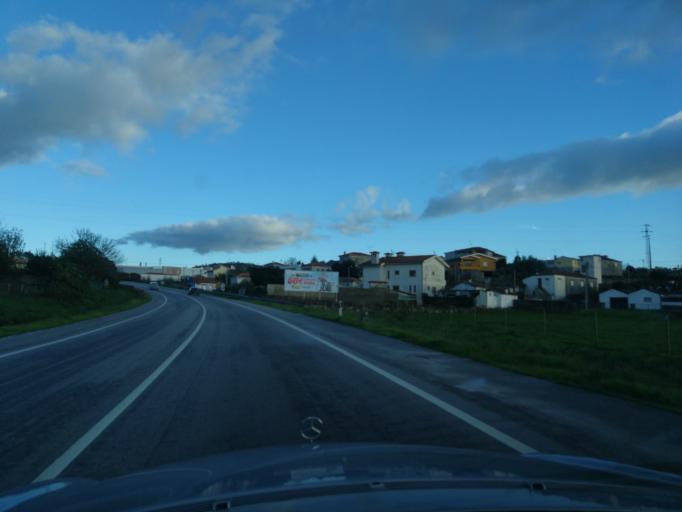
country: PT
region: Braga
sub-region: Barcelos
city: Barcelos
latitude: 41.5150
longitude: -8.6228
